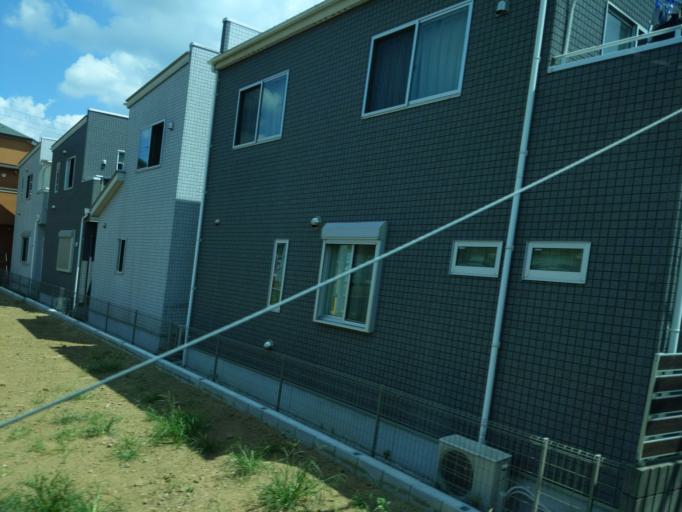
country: JP
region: Tokyo
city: Chofugaoka
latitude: 35.6279
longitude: 139.5578
